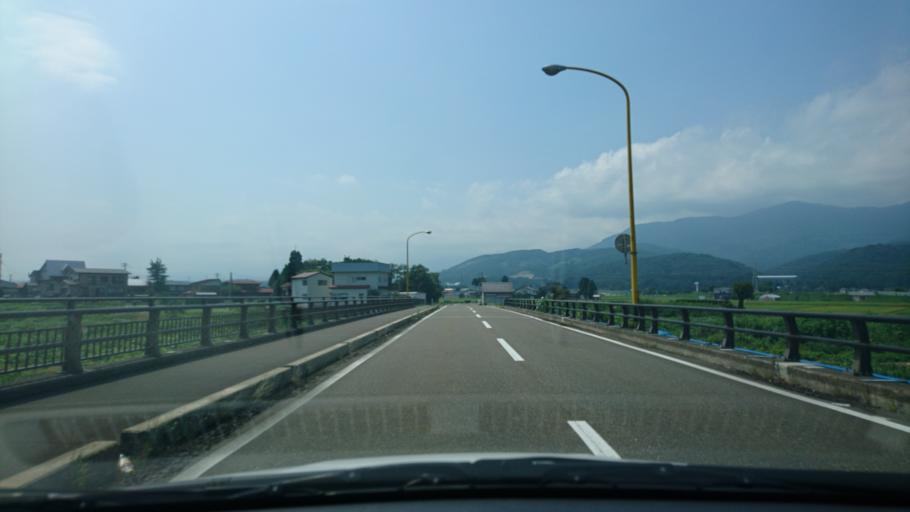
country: JP
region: Niigata
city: Arai
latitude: 37.0525
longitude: 138.2534
